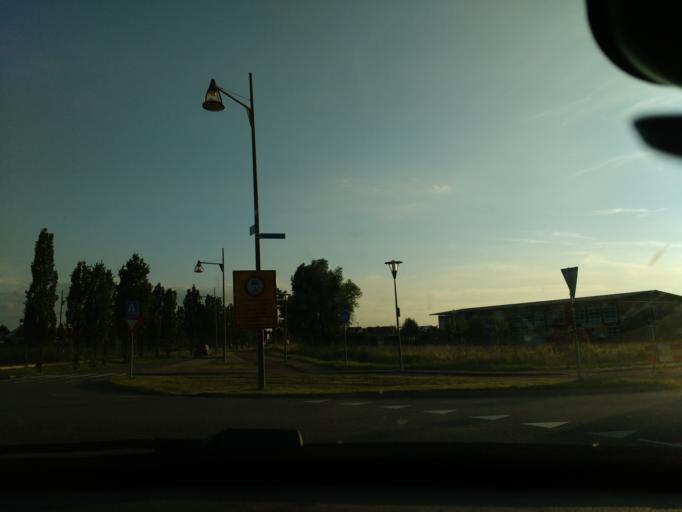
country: NL
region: Gelderland
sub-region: Gemeente Overbetuwe
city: Oosterhout
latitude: 51.8827
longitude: 5.8461
